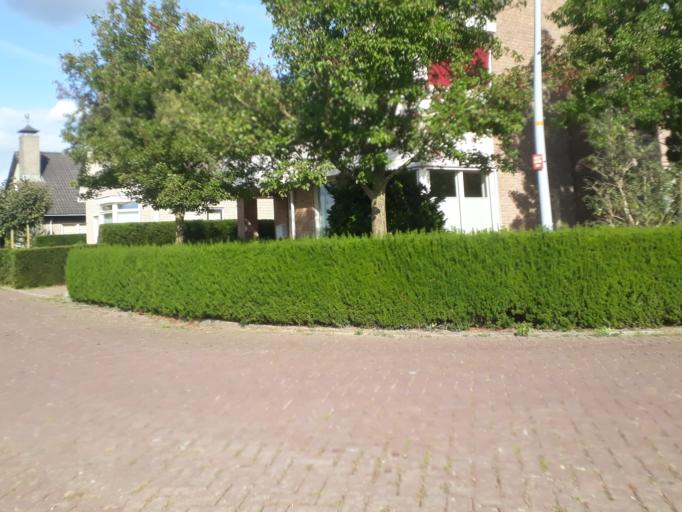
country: NL
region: Gelderland
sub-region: Gemeente Zevenaar
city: Zevenaar
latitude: 51.9349
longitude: 6.0519
